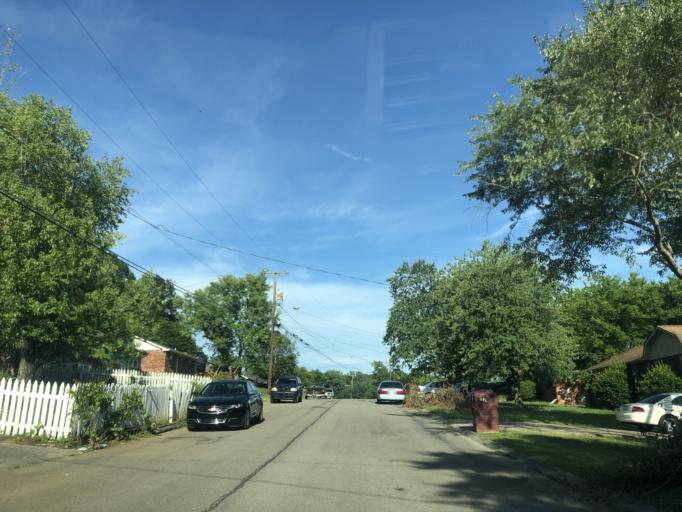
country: US
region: Tennessee
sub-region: Davidson County
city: Nashville
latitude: 36.2241
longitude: -86.8466
